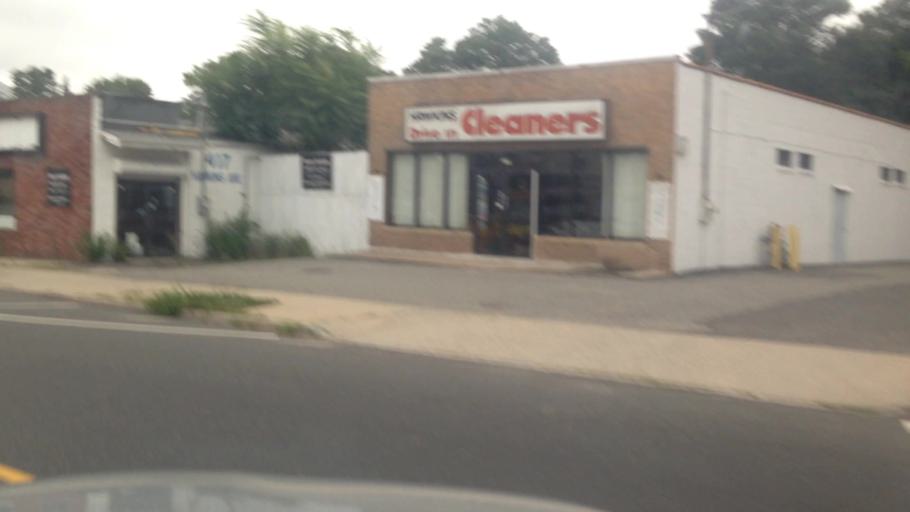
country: US
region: New York
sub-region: Suffolk County
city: Ronkonkoma
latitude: 40.8241
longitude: -73.1076
